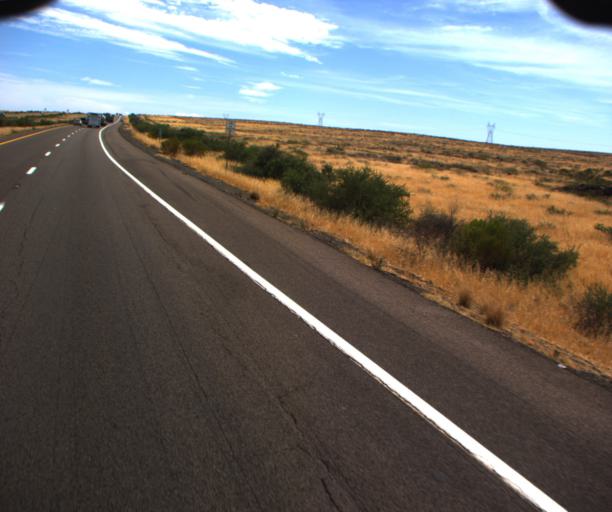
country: US
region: Arizona
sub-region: Yavapai County
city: Cordes Lakes
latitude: 34.1991
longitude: -112.1275
